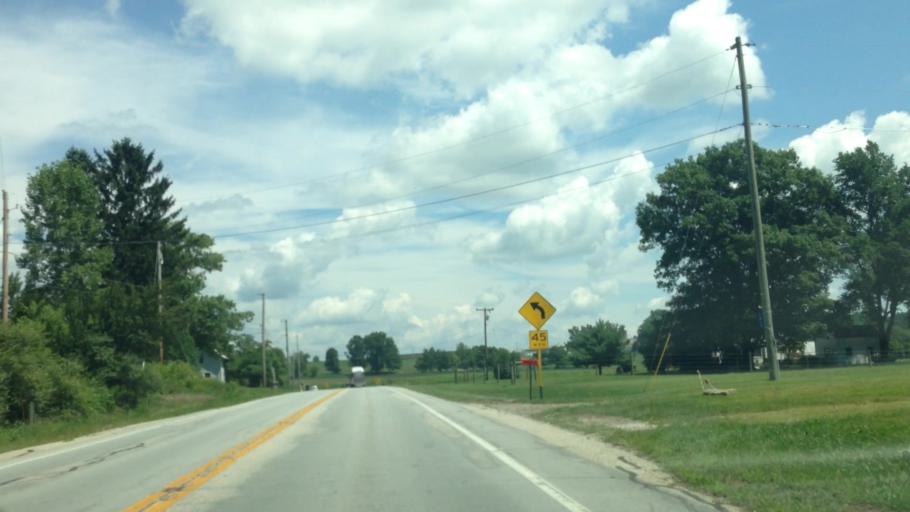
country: US
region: Ohio
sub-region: Wayne County
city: Smithville
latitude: 40.8949
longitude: -81.8111
